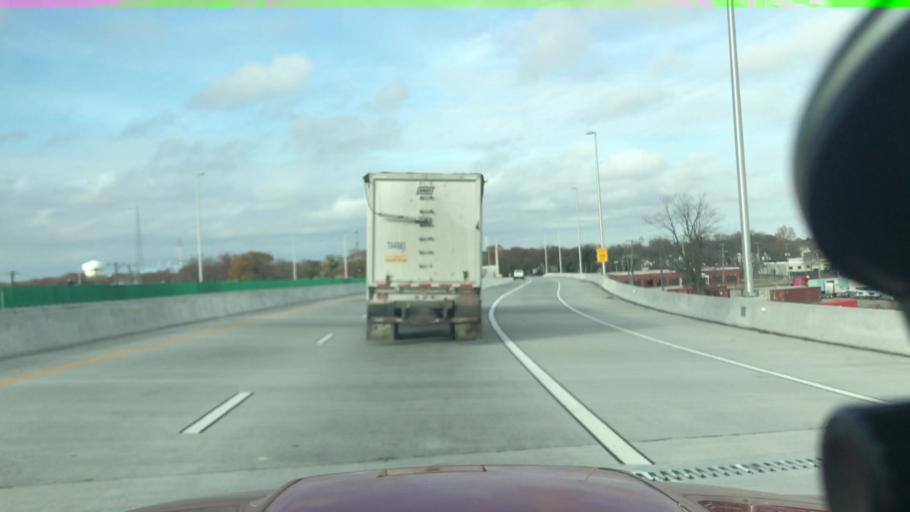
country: US
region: Virginia
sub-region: City of Portsmouth
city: Portsmouth
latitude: 36.8307
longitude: -76.3268
